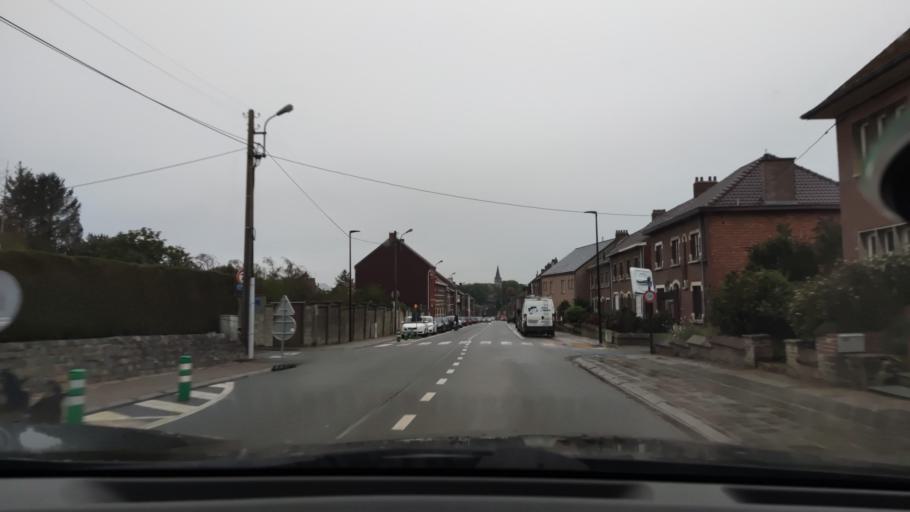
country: BE
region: Wallonia
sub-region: Province du Brabant Wallon
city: Jodoigne
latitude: 50.7241
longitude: 4.8591
